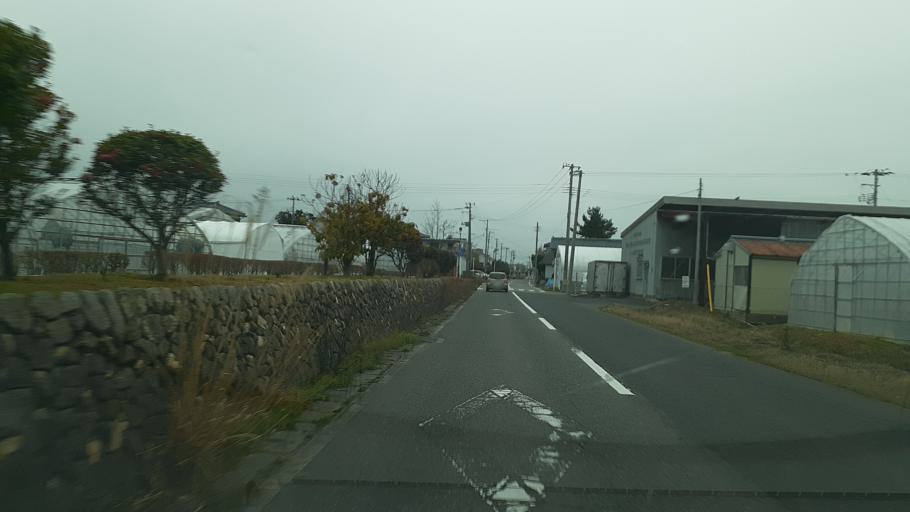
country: JP
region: Niigata
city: Niigata-shi
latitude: 37.8617
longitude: 139.0364
